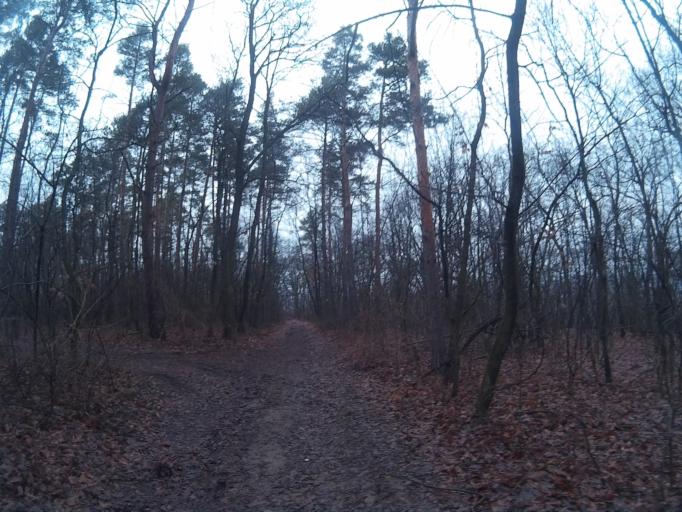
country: HU
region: Komarom-Esztergom
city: Tat
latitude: 47.7242
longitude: 18.6079
